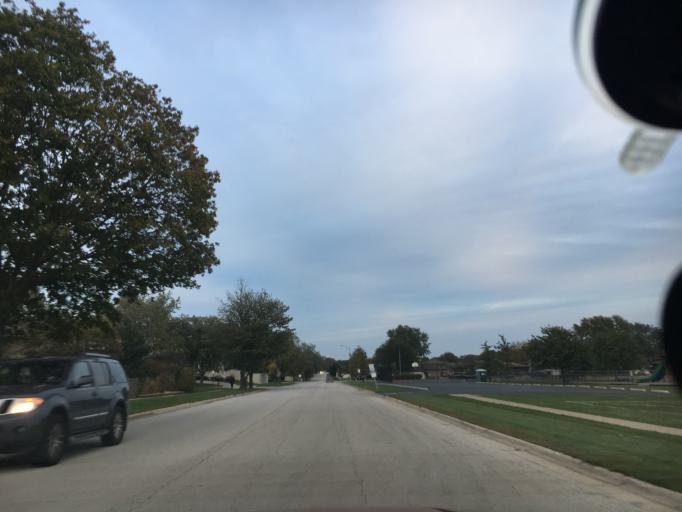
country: US
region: Illinois
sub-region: Cook County
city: Oak Forest
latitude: 41.6098
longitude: -87.7779
